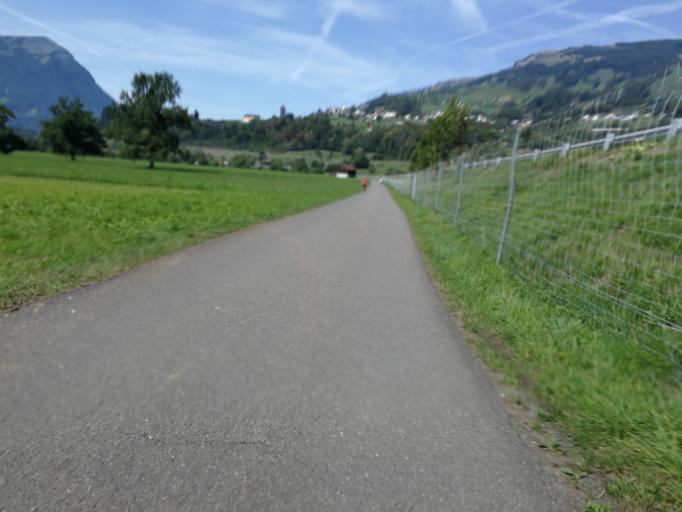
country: CH
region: Schwyz
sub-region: Bezirk Schwyz
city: Steinen
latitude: 47.0446
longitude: 8.5993
